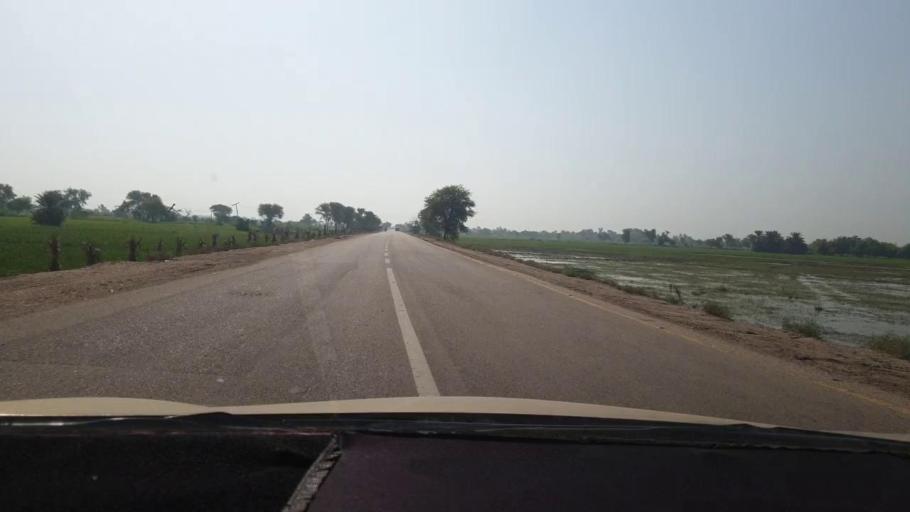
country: PK
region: Sindh
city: Miro Khan
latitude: 27.7298
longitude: 68.1306
